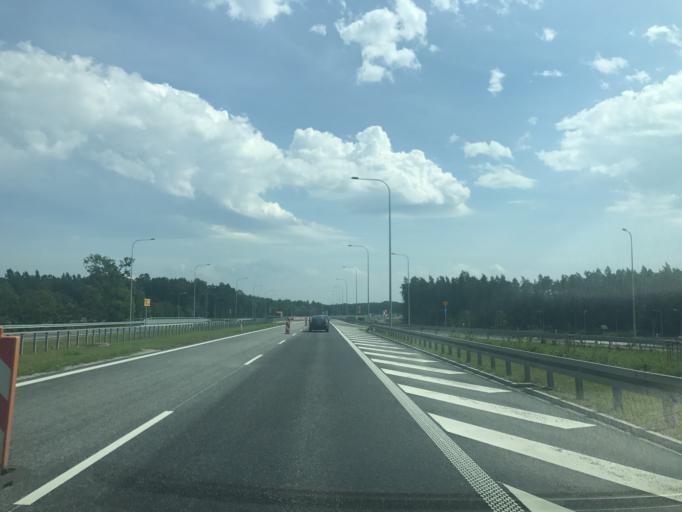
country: PL
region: Warmian-Masurian Voivodeship
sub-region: Powiat ostrodzki
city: Ostroda
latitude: 53.7296
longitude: 19.9343
